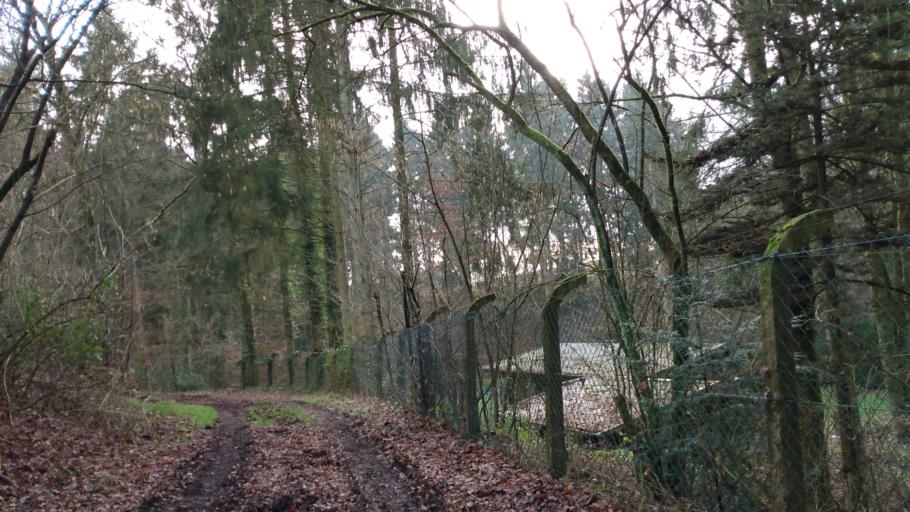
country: DE
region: Rheinland-Pfalz
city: Asbach
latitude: 50.6789
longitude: 7.4456
